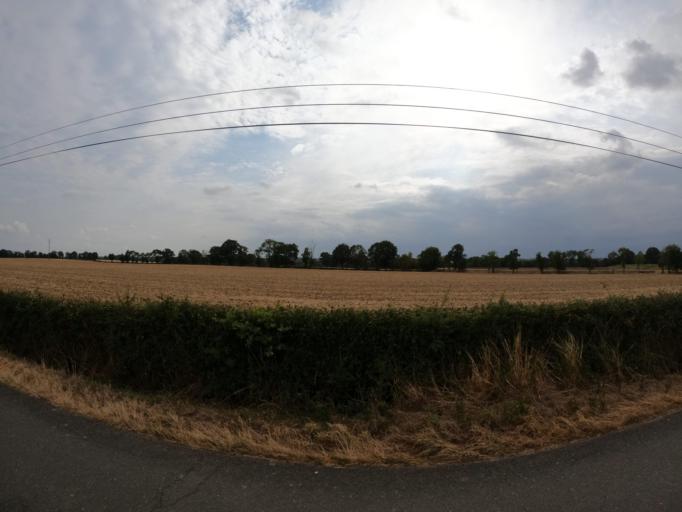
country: FR
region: Pays de la Loire
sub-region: Departement de Maine-et-Loire
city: Saint-Christophe-du-Bois
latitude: 47.0339
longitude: -0.9597
